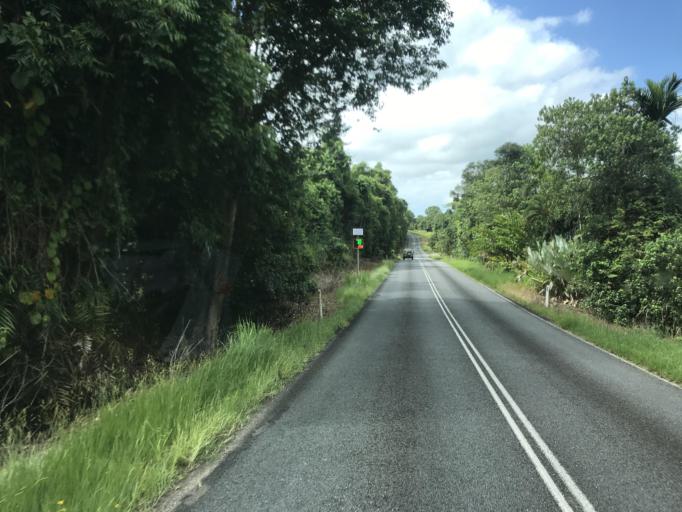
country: AU
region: Queensland
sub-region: Cassowary Coast
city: Innisfail
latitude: -17.8330
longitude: 146.0534
